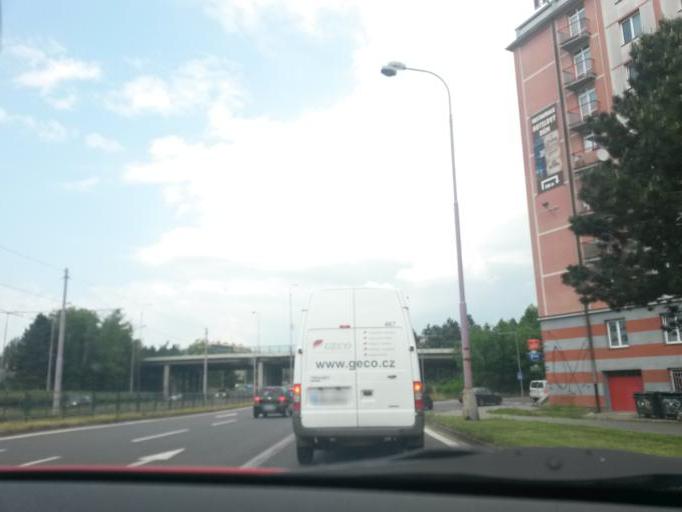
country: CZ
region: Olomoucky
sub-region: Okres Olomouc
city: Olomouc
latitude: 49.5827
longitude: 17.2413
